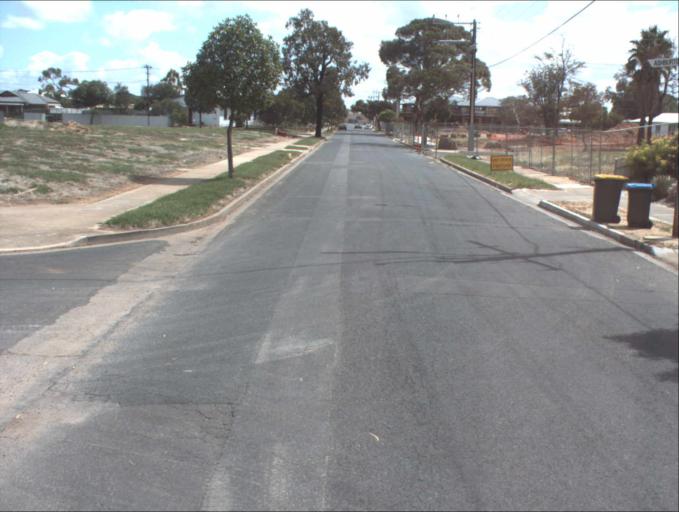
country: AU
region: South Australia
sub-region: Port Adelaide Enfield
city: Enfield
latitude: -34.8517
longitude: 138.5980
